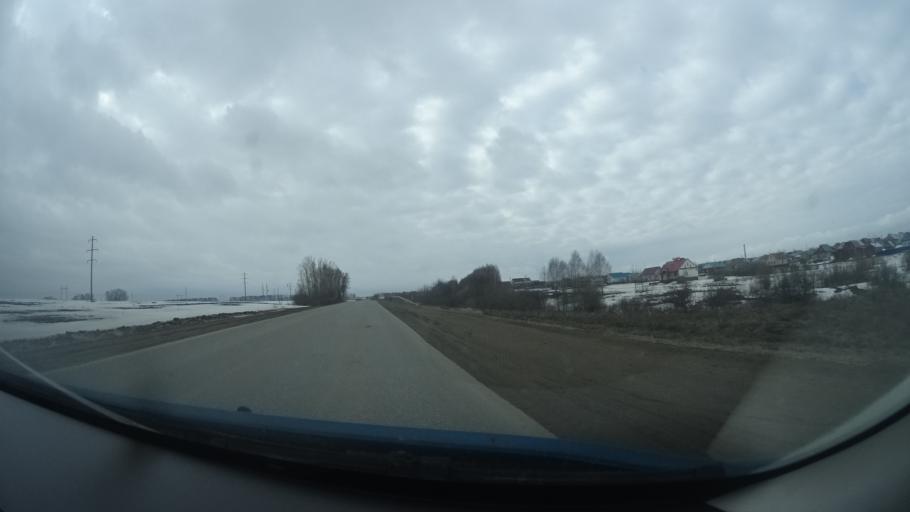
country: RU
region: Bashkortostan
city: Birsk
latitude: 55.4506
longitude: 55.5905
